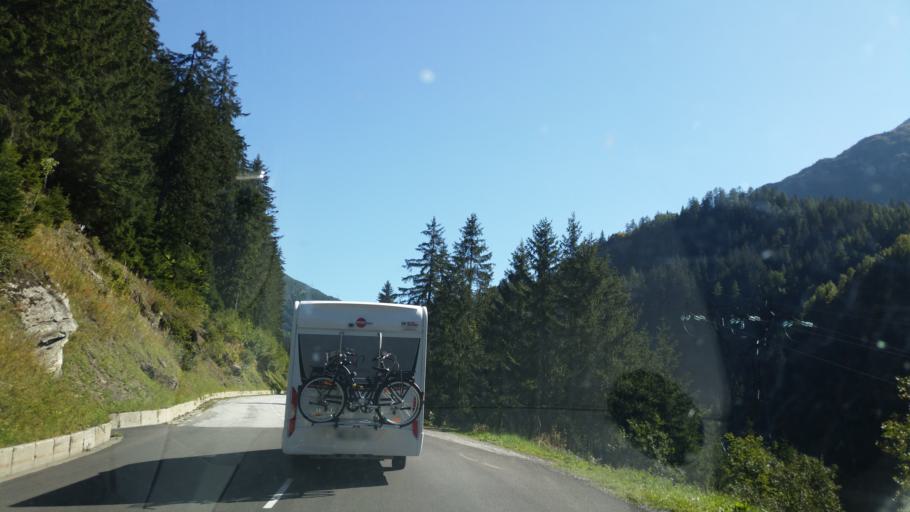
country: FR
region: Rhone-Alpes
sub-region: Departement de la Savoie
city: Tignes
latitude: 45.5527
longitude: 6.9015
